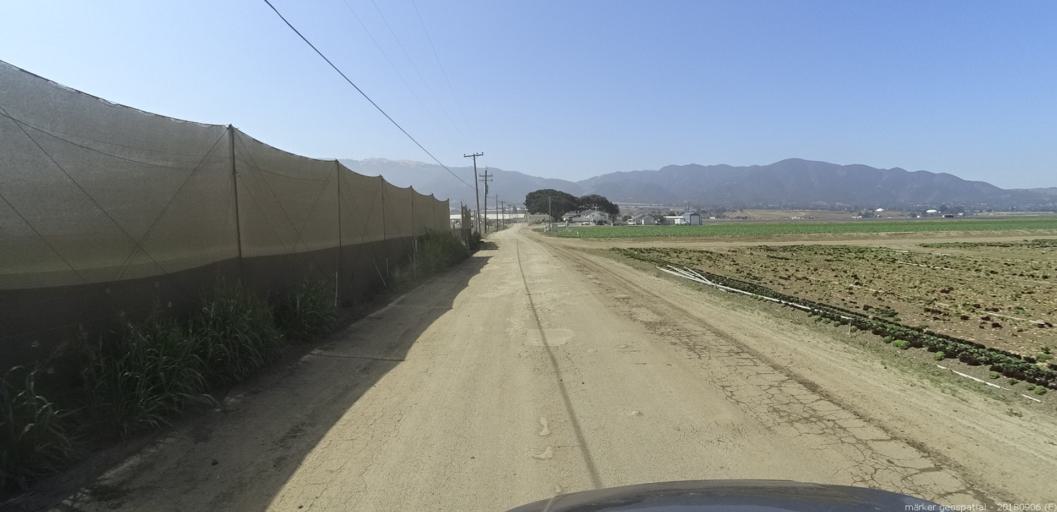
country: US
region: California
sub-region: Monterey County
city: Chualar
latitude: 36.6027
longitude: -121.6015
